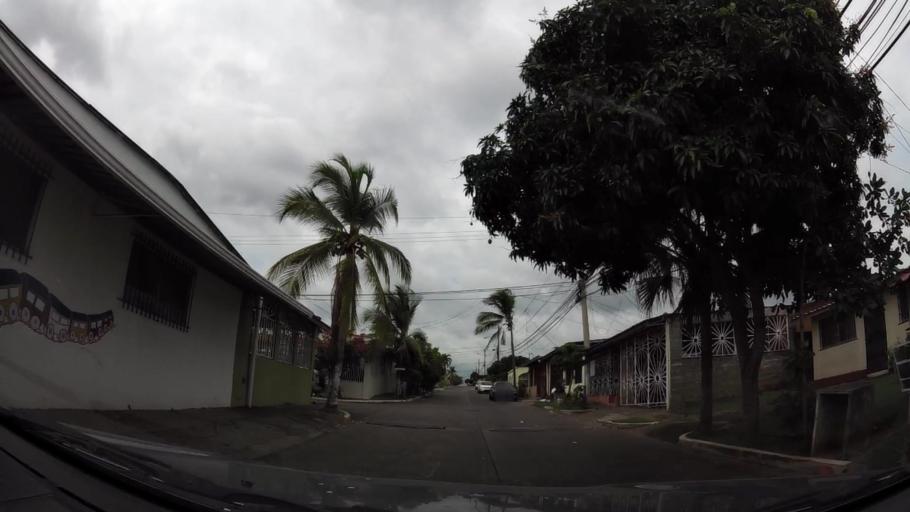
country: PA
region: Panama
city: San Miguelito
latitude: 9.0543
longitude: -79.4210
